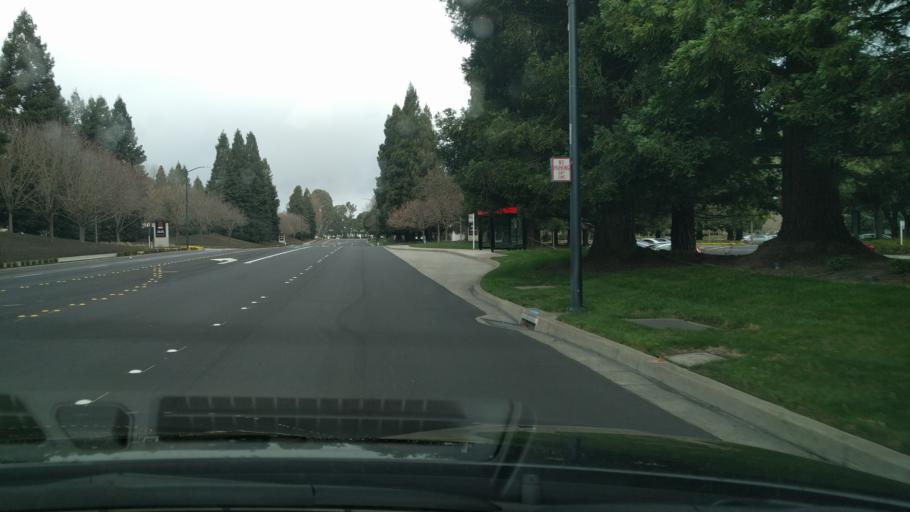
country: US
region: California
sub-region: Contra Costa County
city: San Ramon
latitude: 37.7711
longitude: -121.9625
